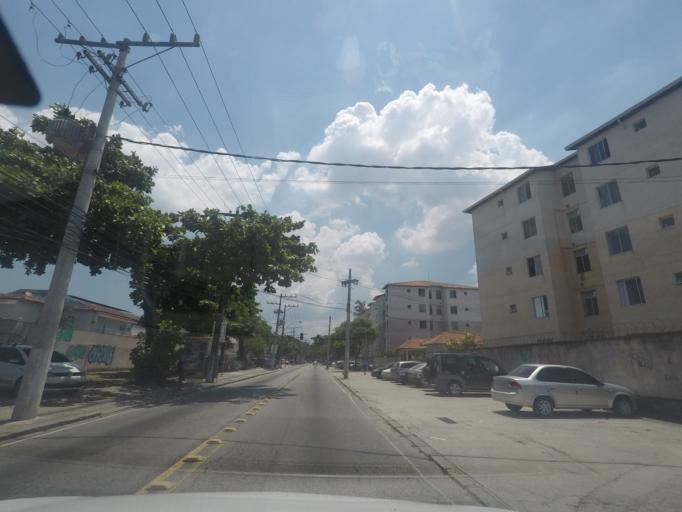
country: BR
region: Rio de Janeiro
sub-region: Duque De Caxias
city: Duque de Caxias
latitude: -22.8236
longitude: -43.3093
